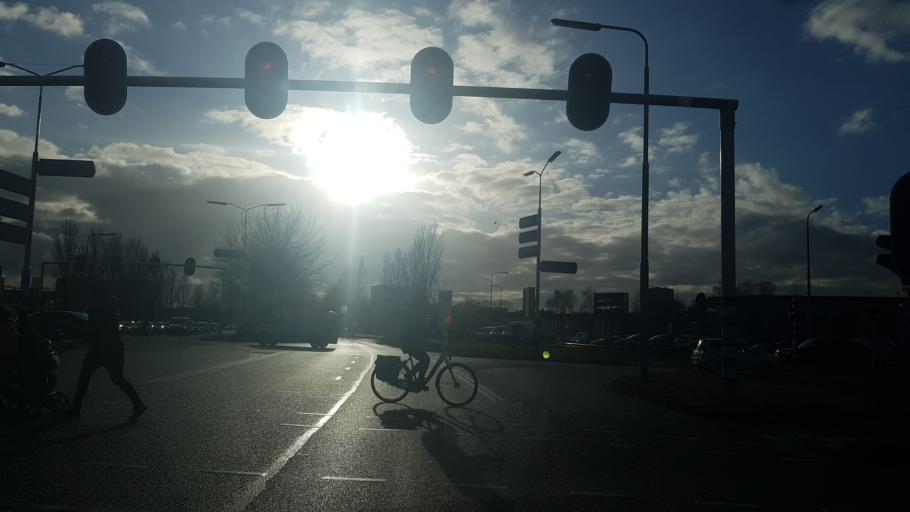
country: NL
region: Friesland
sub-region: Gemeente Leeuwarden
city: Leeuwarden
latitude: 53.2136
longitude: 5.8140
